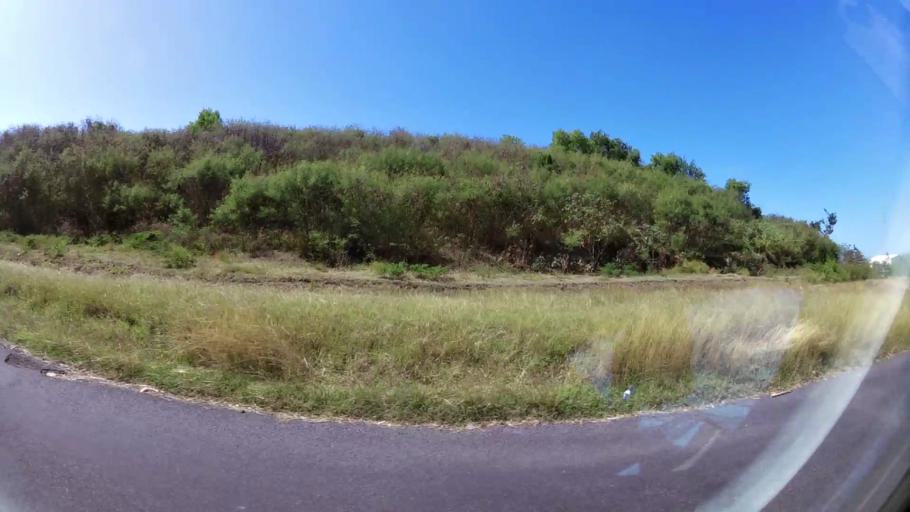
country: YT
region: Pamandzi
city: Pamandzi
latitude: -12.8053
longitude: 45.2833
